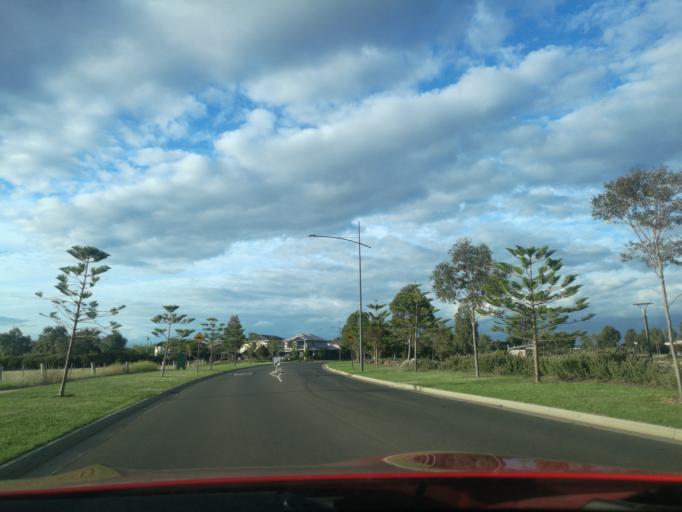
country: AU
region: Victoria
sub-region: Wyndham
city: Point Cook
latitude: -37.9159
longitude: 144.7758
